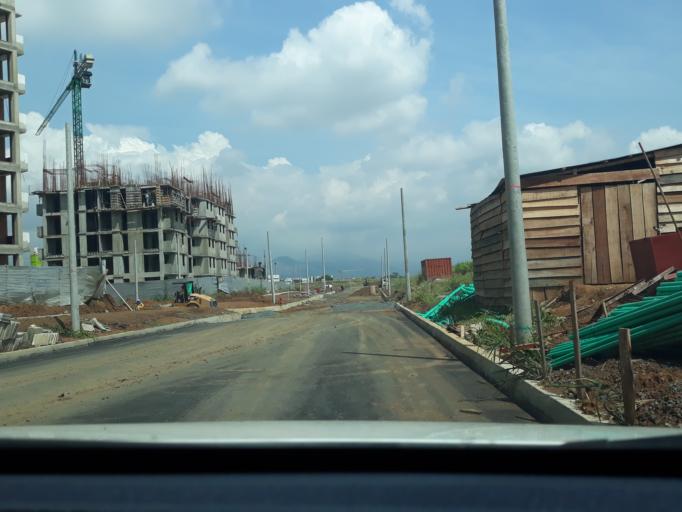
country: CO
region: Valle del Cauca
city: Cali
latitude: 3.3719
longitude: -76.5045
